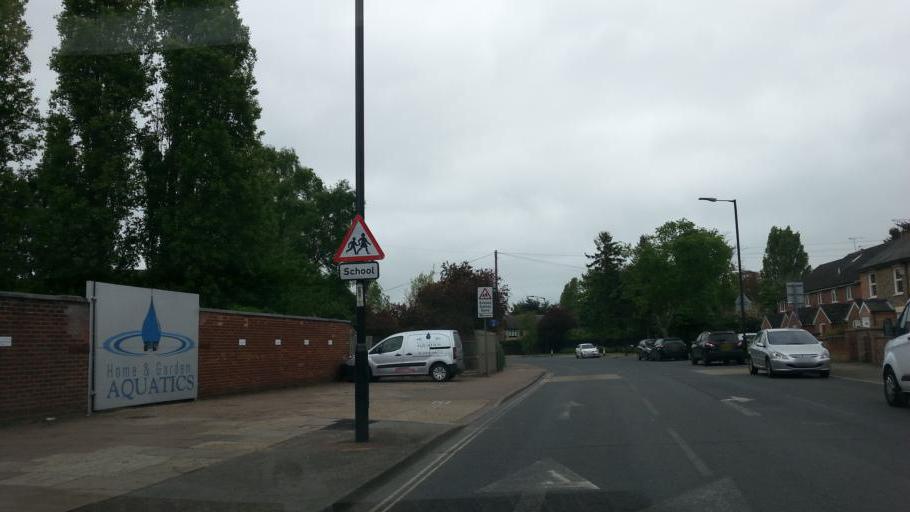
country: GB
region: England
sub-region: Suffolk
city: Bury St Edmunds
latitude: 52.2592
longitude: 0.7049
